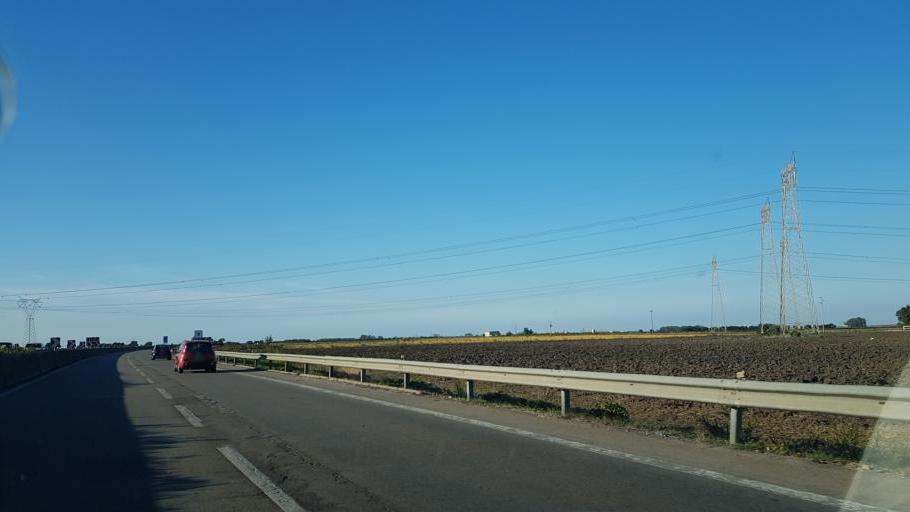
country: IT
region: Apulia
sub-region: Provincia di Brindisi
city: Tuturano
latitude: 40.5568
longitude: 17.9925
